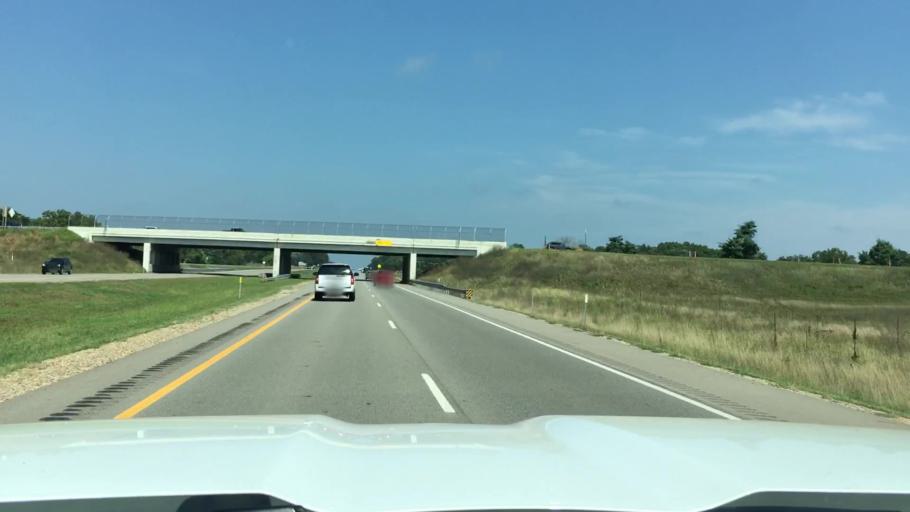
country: US
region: Michigan
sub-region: Kalamazoo County
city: Portage
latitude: 42.1982
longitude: -85.6458
